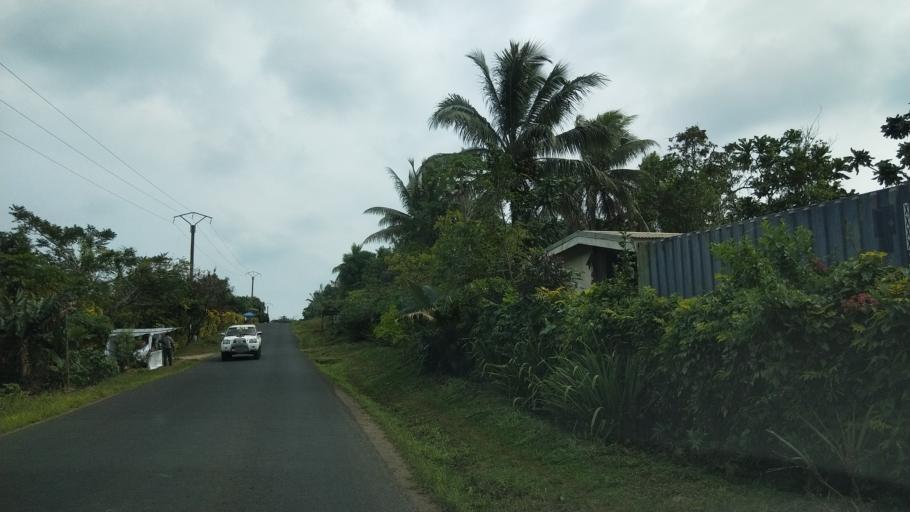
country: VU
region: Shefa
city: Port-Vila
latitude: -17.7309
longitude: 168.3274
